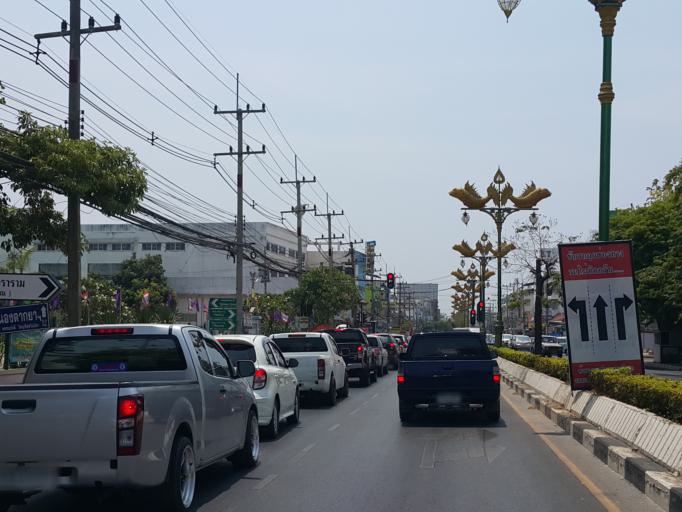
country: TH
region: Kanchanaburi
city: Kanchanaburi
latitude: 14.0309
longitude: 99.5273
